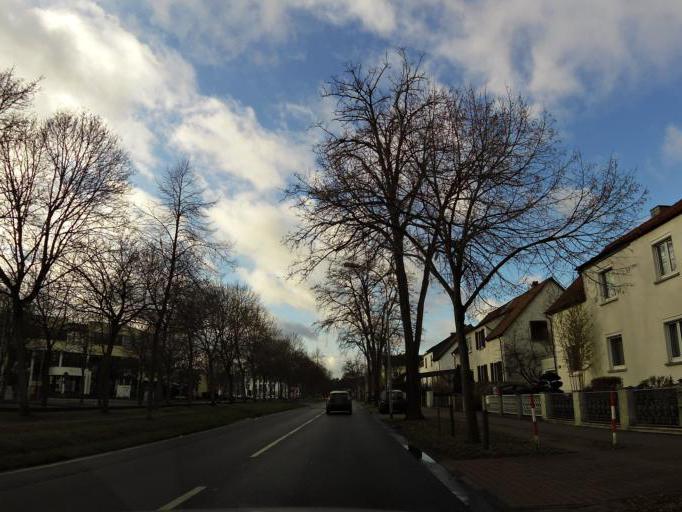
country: DE
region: Hesse
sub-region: Regierungsbezirk Darmstadt
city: Neu Isenburg
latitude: 50.0482
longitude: 8.6819
